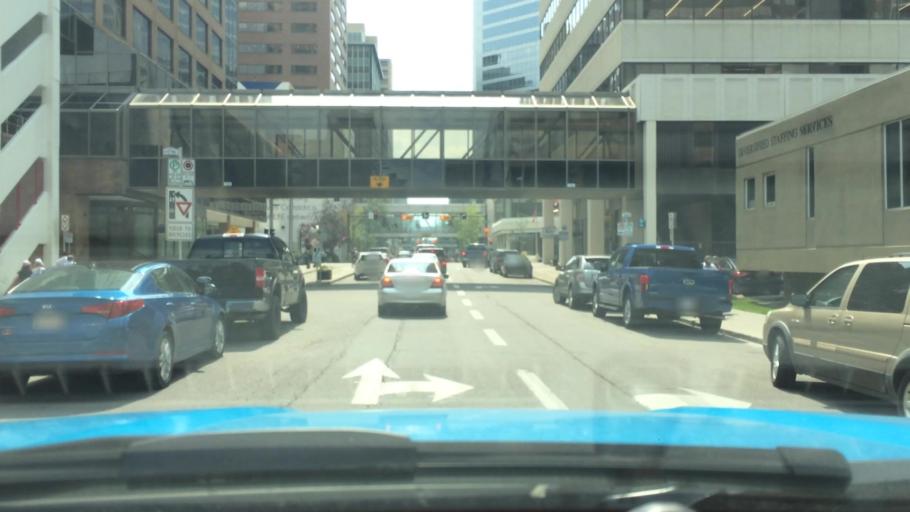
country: CA
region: Alberta
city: Calgary
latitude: 51.0487
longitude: -114.0786
